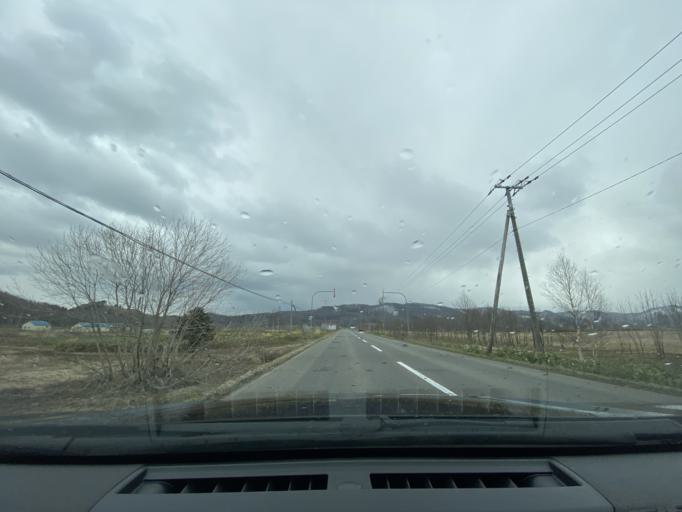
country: JP
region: Hokkaido
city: Nayoro
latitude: 44.1712
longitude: 142.2536
